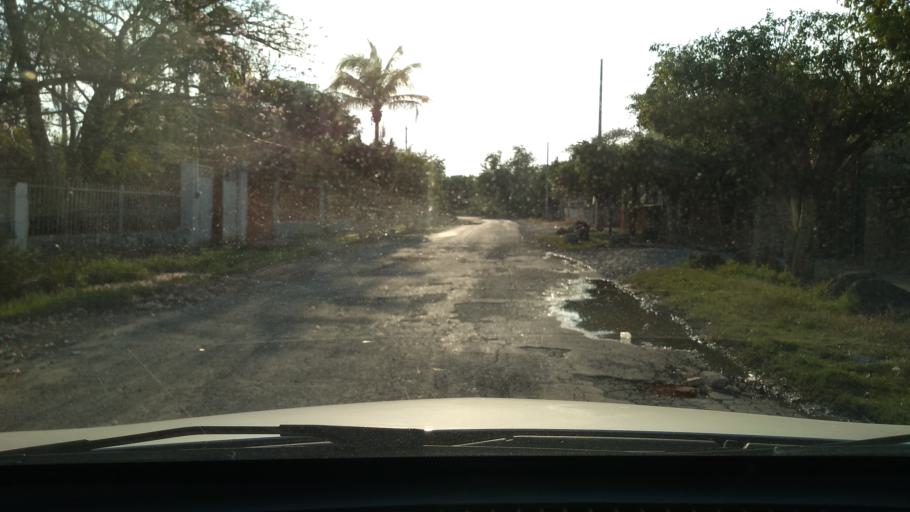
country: MX
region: Morelos
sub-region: Jojutla
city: Tehuixtla
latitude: 18.5636
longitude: -99.2699
